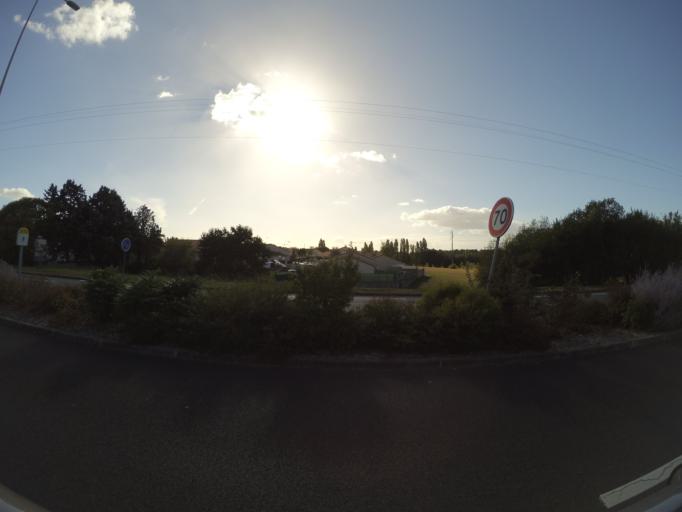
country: FR
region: Pays de la Loire
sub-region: Departement de Maine-et-Loire
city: Cholet
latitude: 47.0546
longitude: -0.9013
